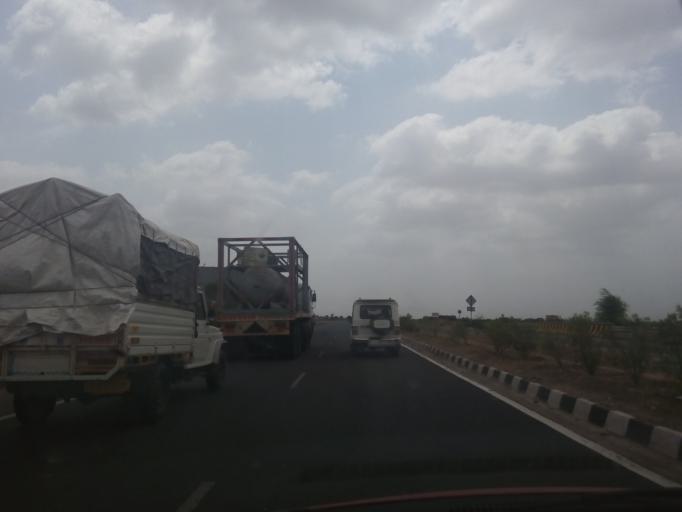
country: IN
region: Gujarat
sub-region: Surendranagar
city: Dhrangadhra
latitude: 23.0031
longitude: 71.5428
